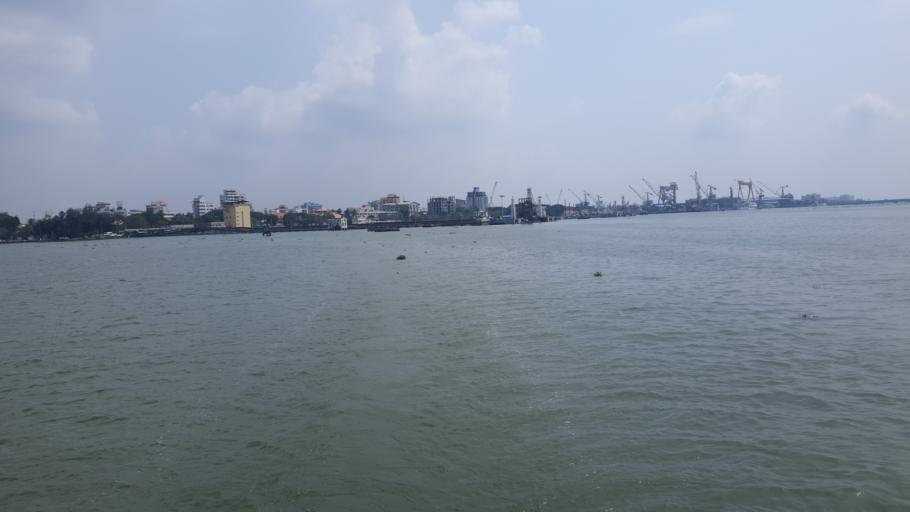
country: IN
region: Kerala
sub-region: Ernakulam
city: Cochin
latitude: 9.9680
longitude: 76.2759
